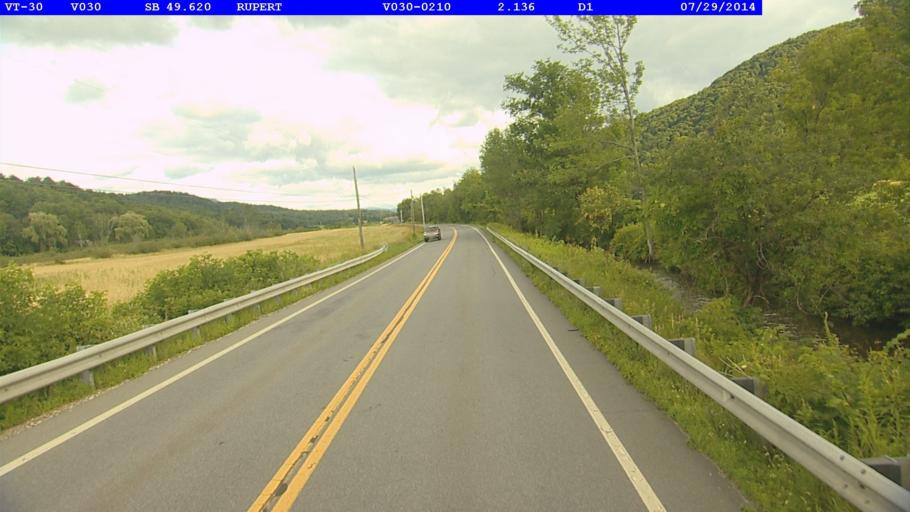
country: US
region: Vermont
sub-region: Bennington County
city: Manchester Center
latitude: 43.2966
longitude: -73.1435
